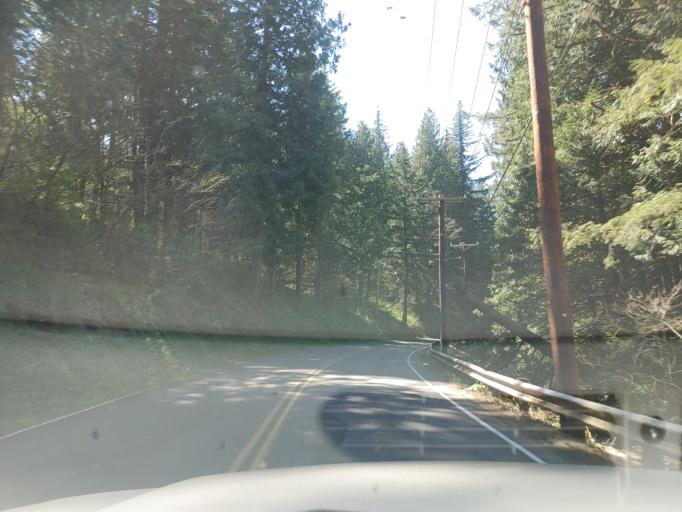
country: US
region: Oregon
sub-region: Multnomah County
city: Troutdale
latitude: 45.5211
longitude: -122.3231
